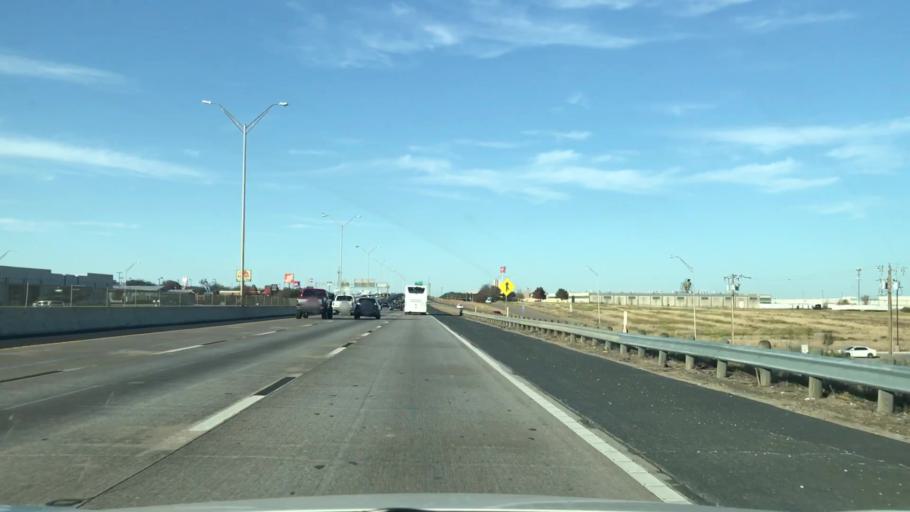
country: US
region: Texas
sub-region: Tarrant County
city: Everman
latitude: 32.6285
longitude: -97.3214
